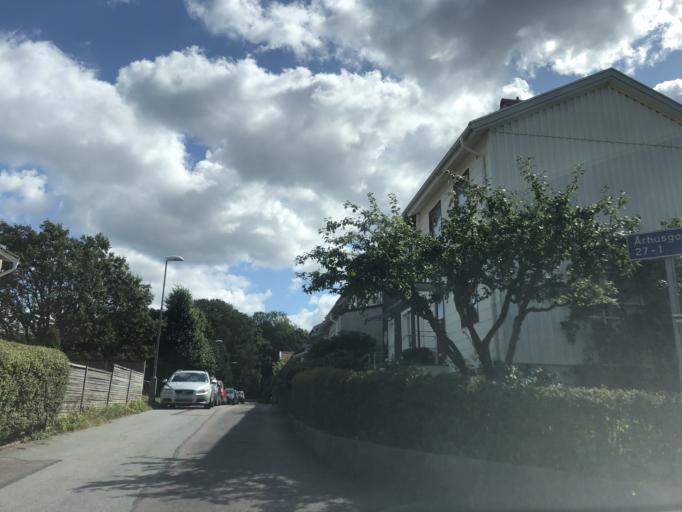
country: SE
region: Vaestra Goetaland
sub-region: Goteborg
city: Majorna
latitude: 57.7035
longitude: 11.9028
